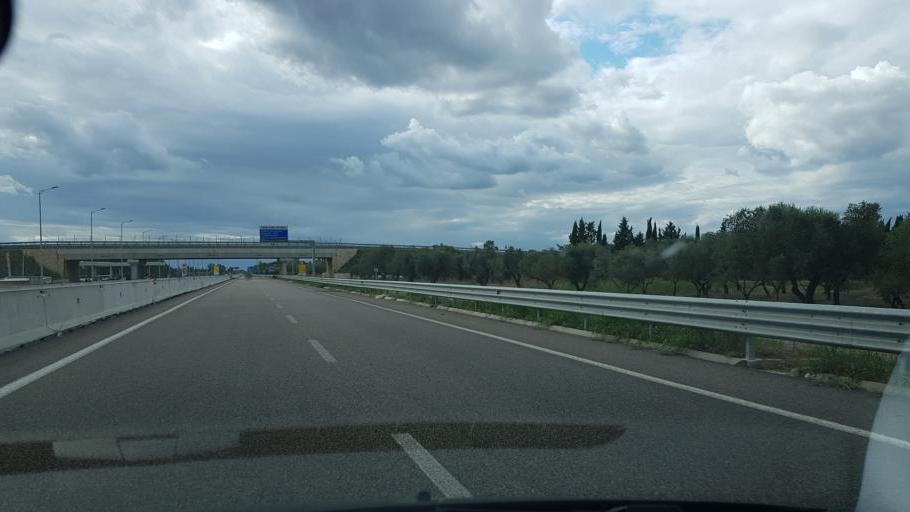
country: IT
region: Apulia
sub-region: Provincia di Lecce
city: Muro Leccese
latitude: 40.1252
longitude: 18.3387
